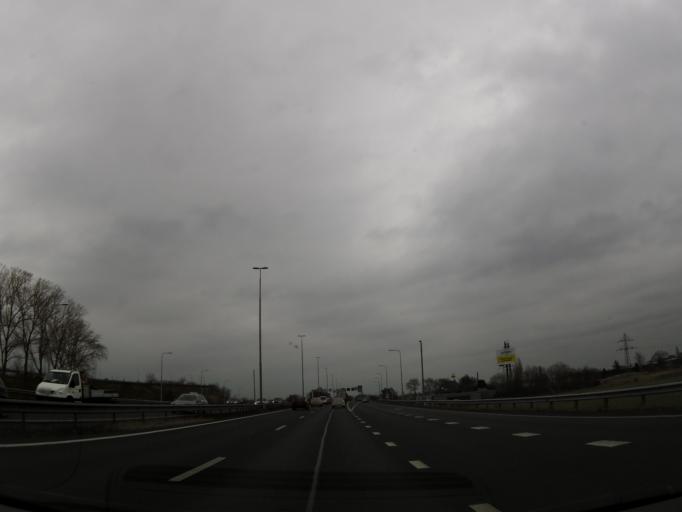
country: NL
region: Limburg
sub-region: Gemeente Maasgouw
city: Maasbracht
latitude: 51.1032
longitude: 5.8488
